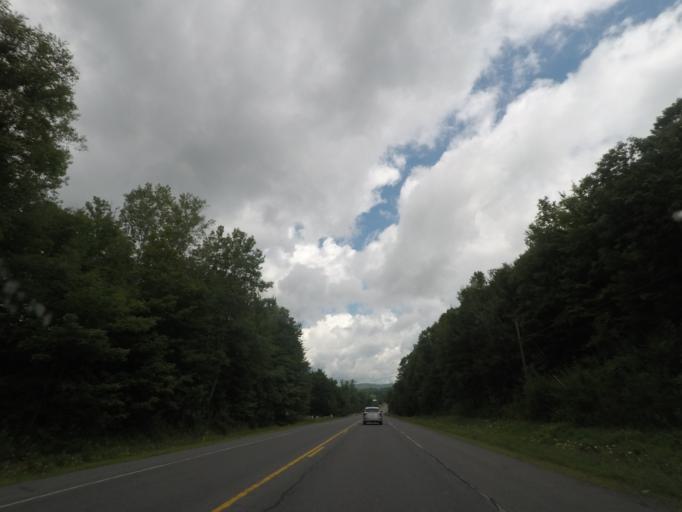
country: US
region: Massachusetts
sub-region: Berkshire County
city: Lanesborough
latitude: 42.5881
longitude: -73.3677
